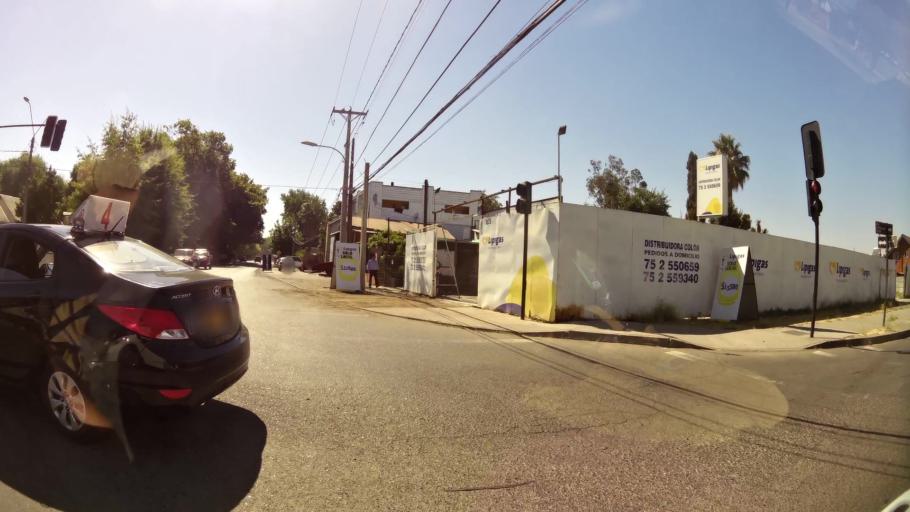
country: CL
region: Maule
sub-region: Provincia de Curico
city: Curico
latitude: -34.9758
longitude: -71.2620
